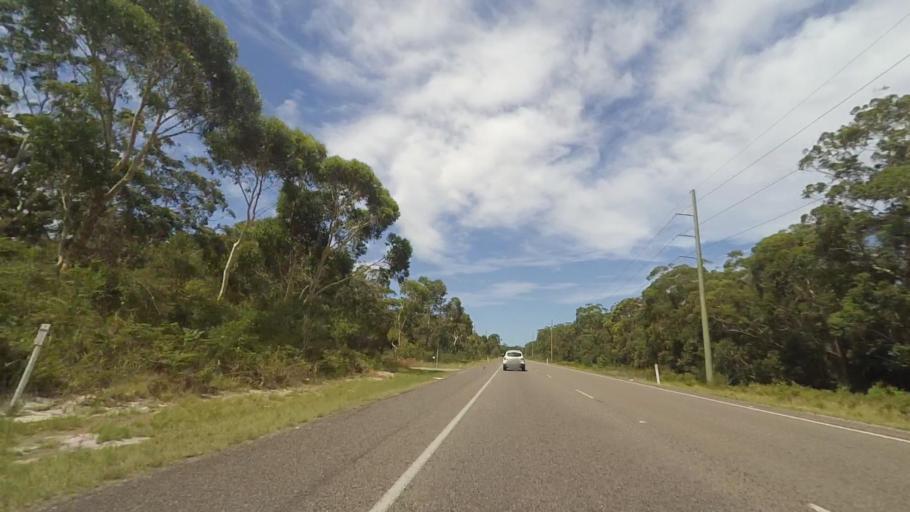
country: AU
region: New South Wales
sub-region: Port Stephens Shire
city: Medowie
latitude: -32.7897
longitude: 151.9590
